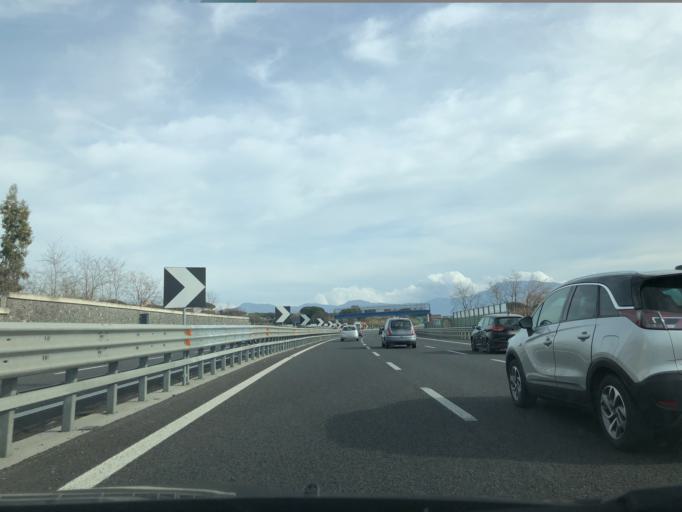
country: IT
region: Campania
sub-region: Provincia di Napoli
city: Torre del Greco
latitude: 40.7858
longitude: 14.3859
